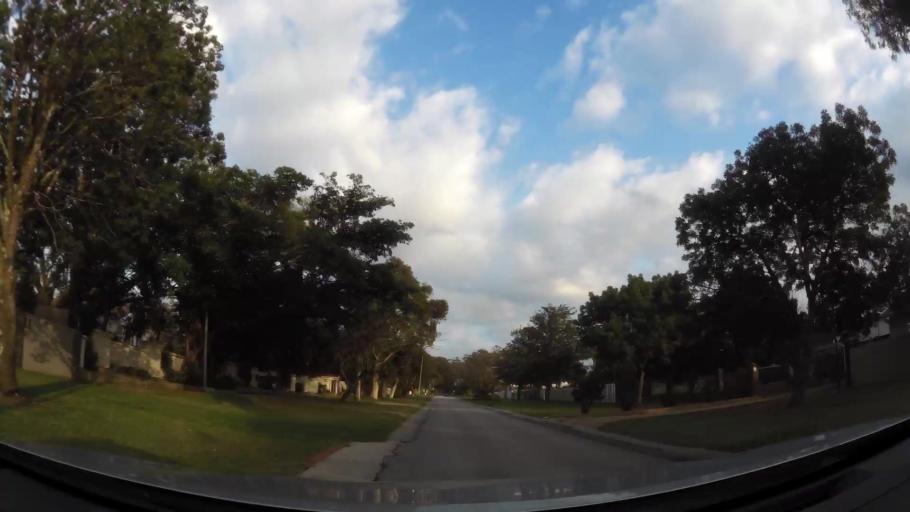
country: ZA
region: Eastern Cape
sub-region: Nelson Mandela Bay Metropolitan Municipality
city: Port Elizabeth
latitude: -33.9791
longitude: 25.5663
